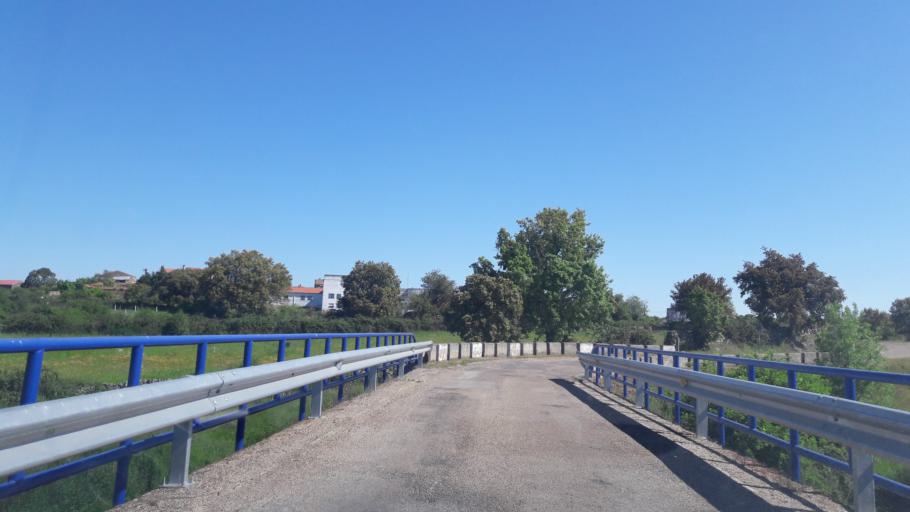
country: ES
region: Castille and Leon
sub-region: Provincia de Salamanca
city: Banobarez
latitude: 40.8717
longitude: -6.5736
